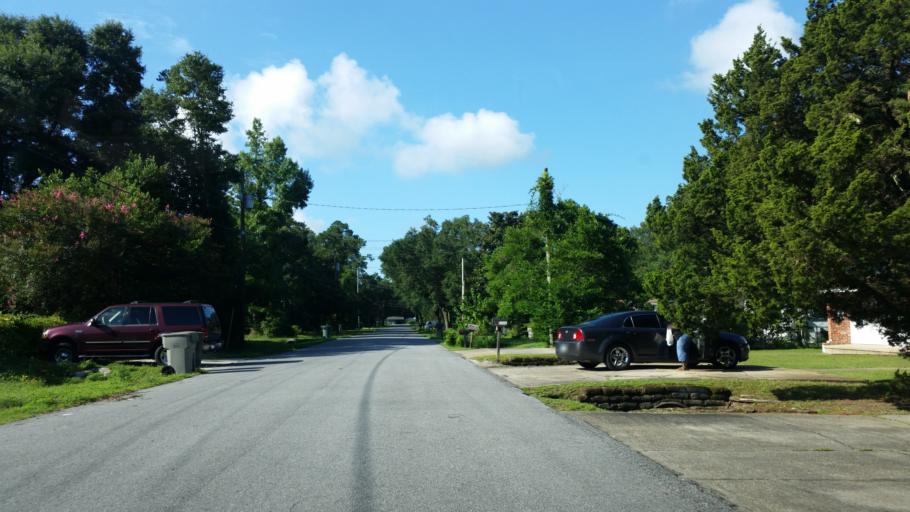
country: US
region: Florida
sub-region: Escambia County
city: Ferry Pass
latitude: 30.5093
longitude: -87.2284
